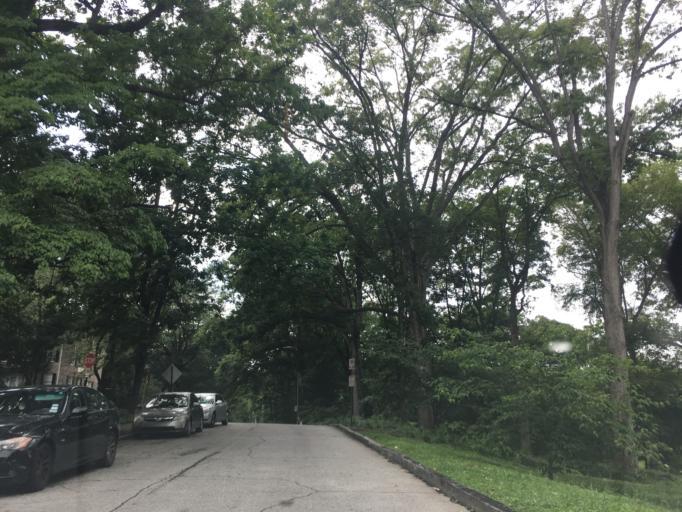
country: US
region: Georgia
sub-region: Fulton County
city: Atlanta
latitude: 33.7901
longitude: -84.3788
